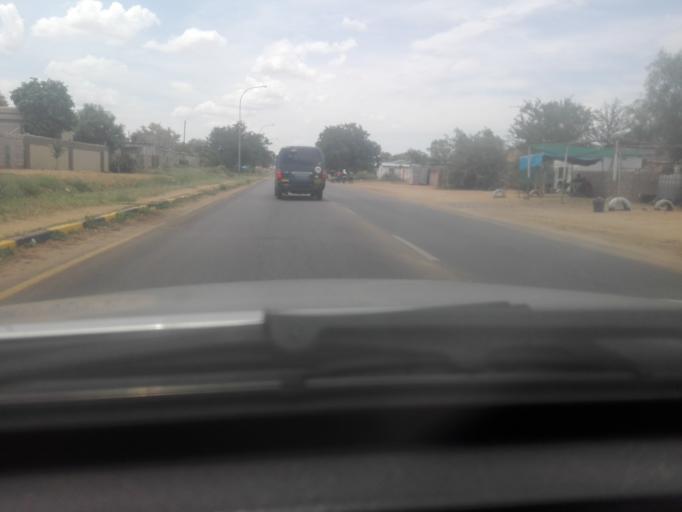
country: BW
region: South East
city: Gaborone
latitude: -24.6246
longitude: 25.9434
